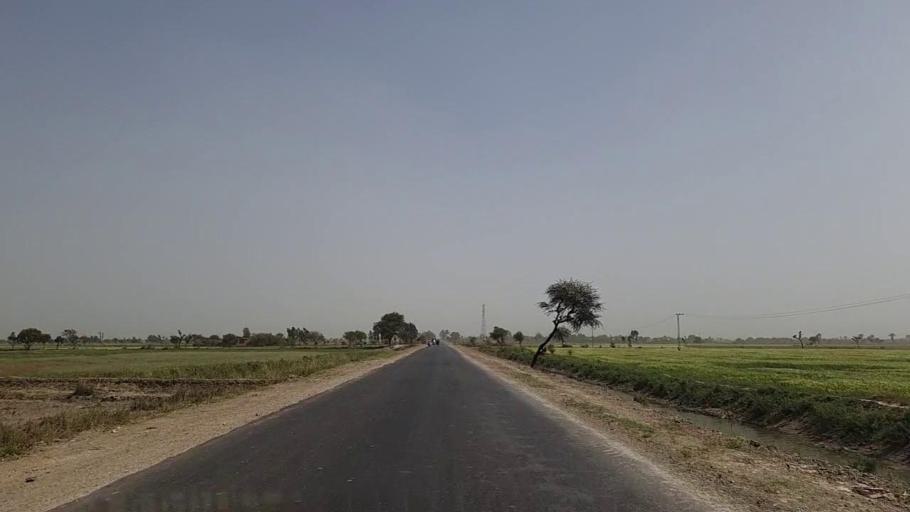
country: PK
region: Sindh
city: Tando Bago
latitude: 24.8213
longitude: 68.9024
